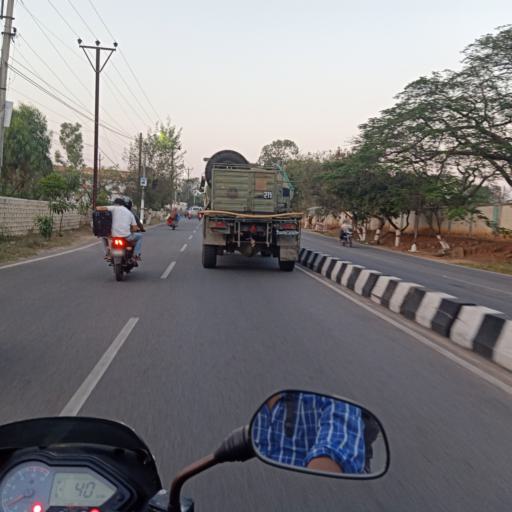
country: IN
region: Telangana
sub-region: Rangareddi
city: Secunderabad
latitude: 17.4834
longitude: 78.5112
